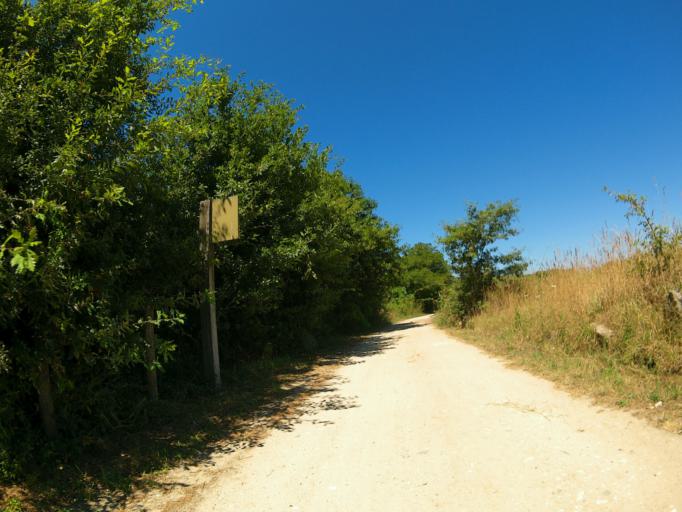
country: PT
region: Viana do Castelo
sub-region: Viana do Castelo
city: Darque
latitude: 41.7146
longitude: -8.7046
